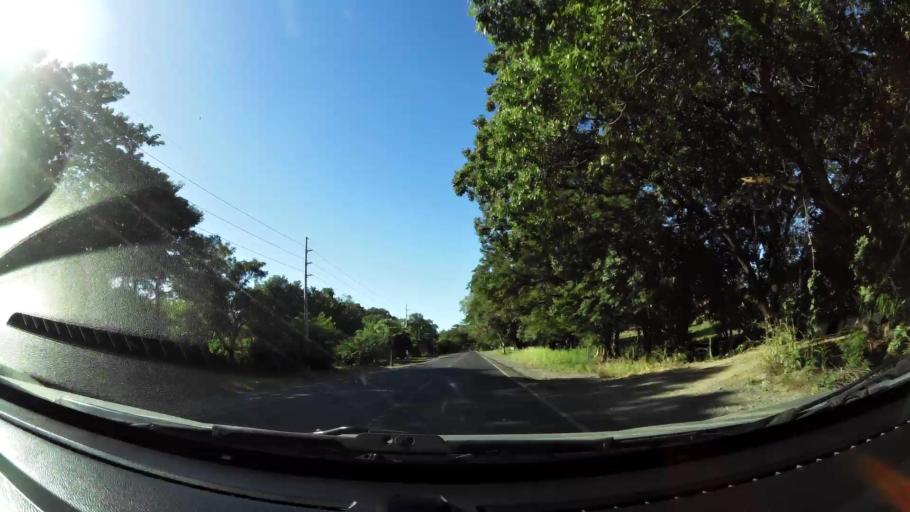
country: CR
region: Guanacaste
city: Belen
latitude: 10.4178
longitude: -85.5755
